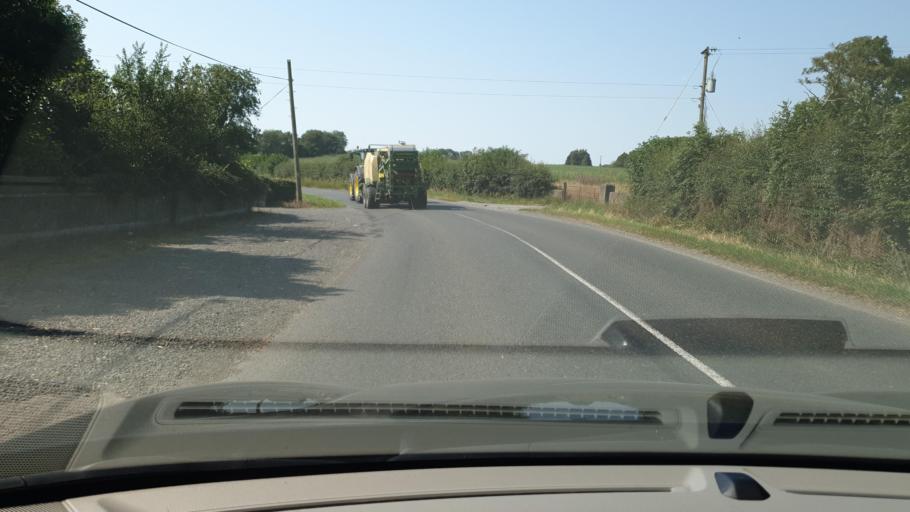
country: IE
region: Leinster
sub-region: An Mhi
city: Athboy
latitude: 53.5920
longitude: -6.8611
